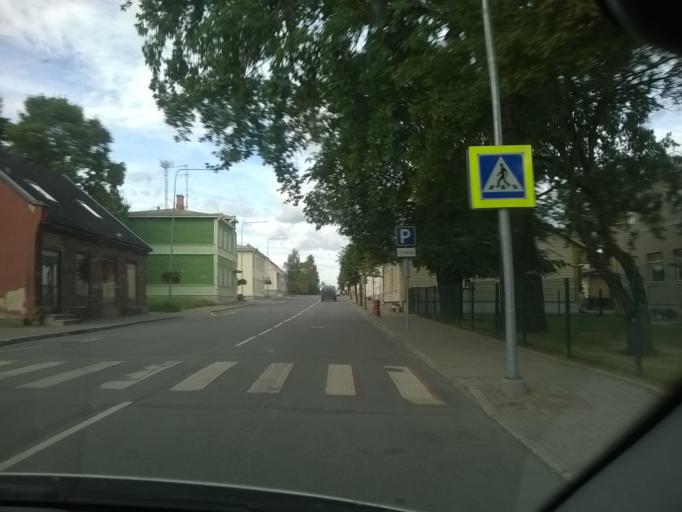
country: EE
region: Vorumaa
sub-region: Voru linn
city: Voru
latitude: 57.8451
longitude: 26.9972
